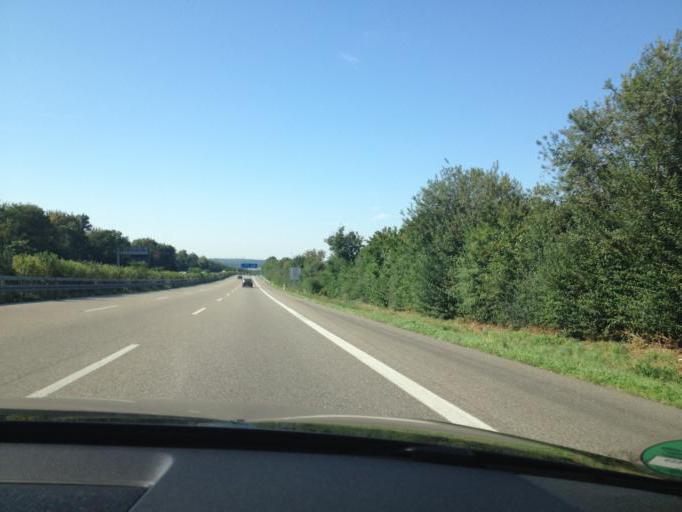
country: DE
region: Baden-Wuerttemberg
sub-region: Regierungsbezirk Stuttgart
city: Abstatt
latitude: 49.0721
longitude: 9.2818
